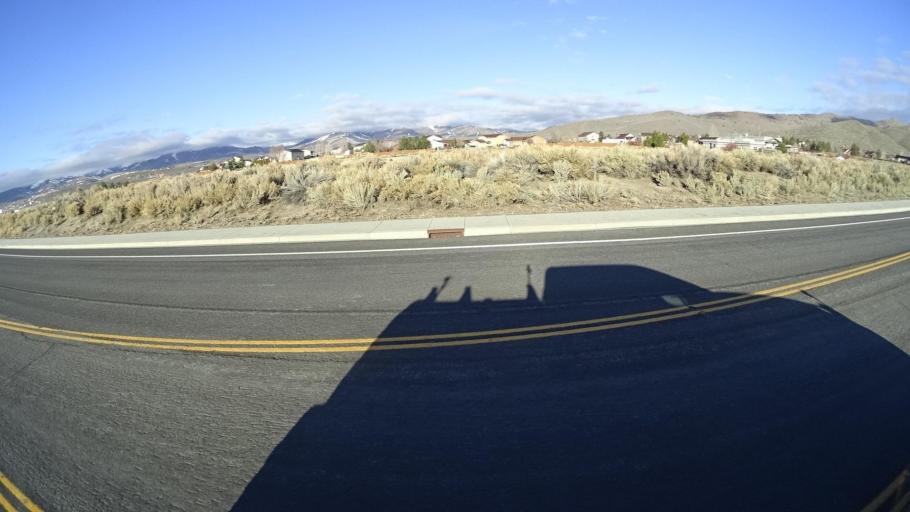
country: US
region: Nevada
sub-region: Washoe County
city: Cold Springs
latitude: 39.6767
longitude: -119.9788
